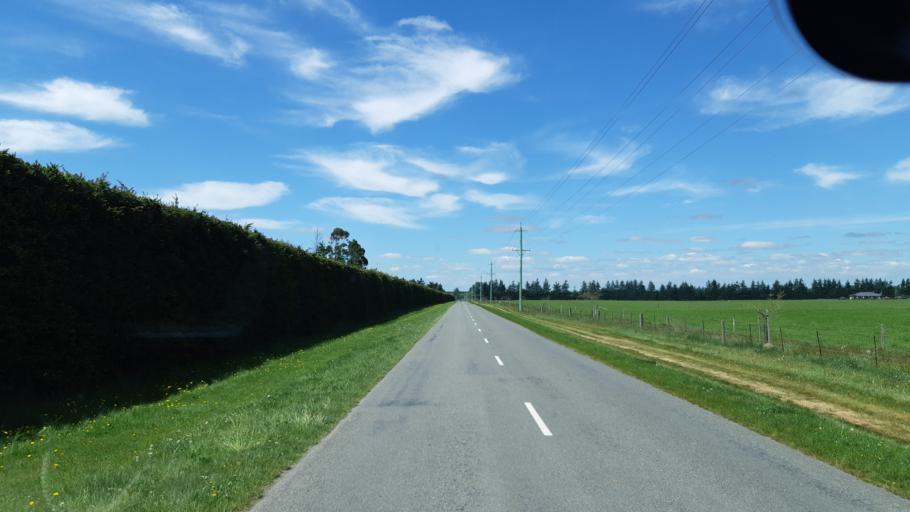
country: NZ
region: Canterbury
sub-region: Ashburton District
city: Methven
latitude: -43.7270
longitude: 171.4994
